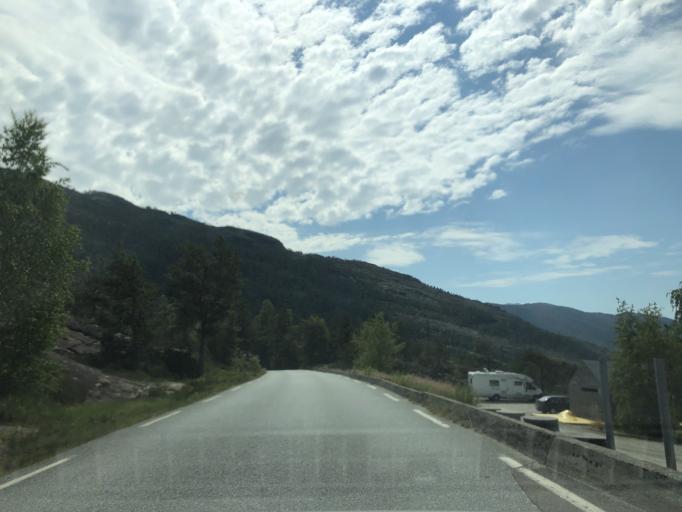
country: NO
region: Hordaland
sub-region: Jondal
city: Jondal
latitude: 60.3288
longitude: 6.3383
